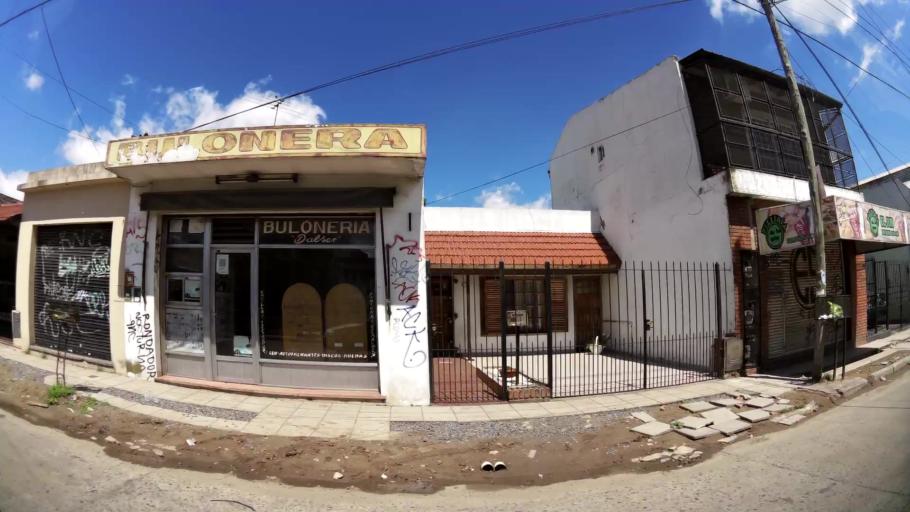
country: AR
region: Buenos Aires
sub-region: Partido de Lanus
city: Lanus
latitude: -34.7031
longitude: -58.4168
